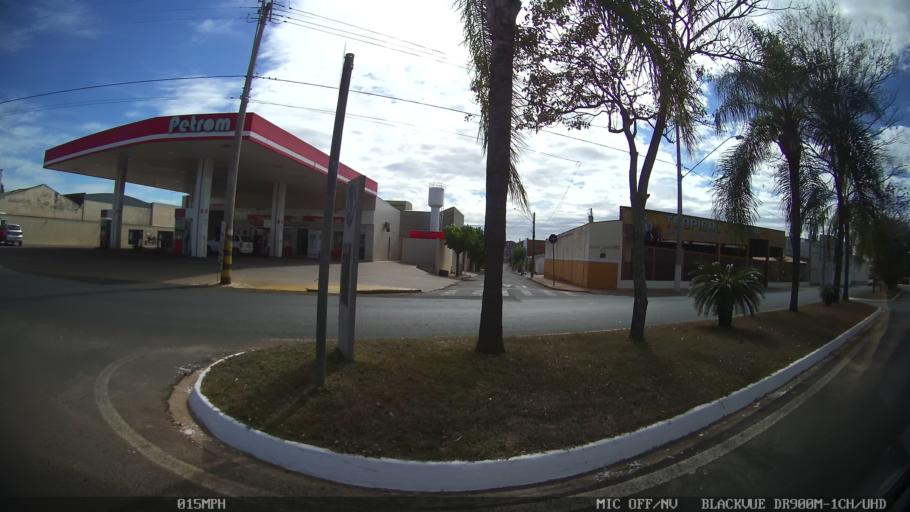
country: BR
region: Sao Paulo
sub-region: Bady Bassitt
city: Bady Bassitt
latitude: -20.8253
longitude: -49.5250
